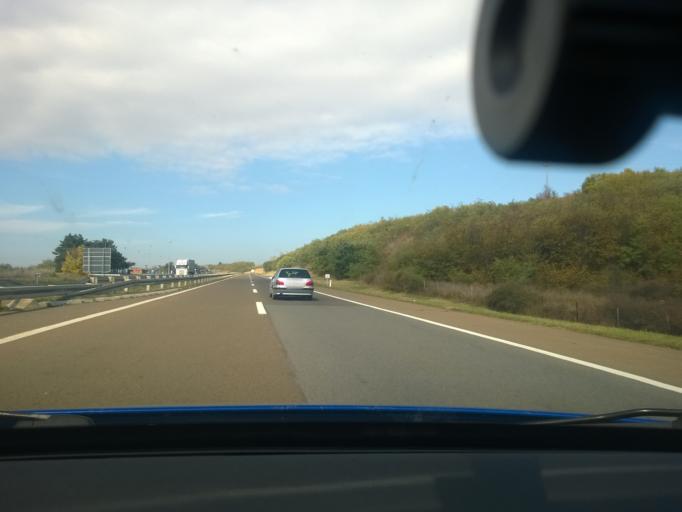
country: RS
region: Central Serbia
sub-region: Nisavski Okrug
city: Aleksinac
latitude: 43.5713
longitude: 21.6742
